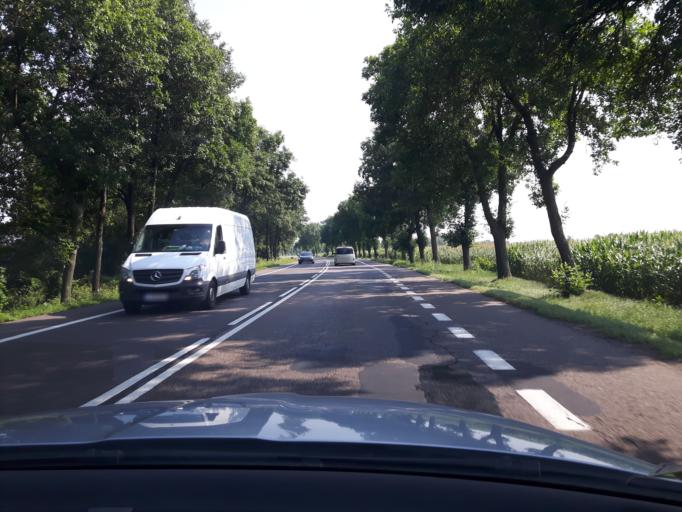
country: PL
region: Masovian Voivodeship
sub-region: Powiat mlawski
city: Strzegowo
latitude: 52.8761
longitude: 20.2887
